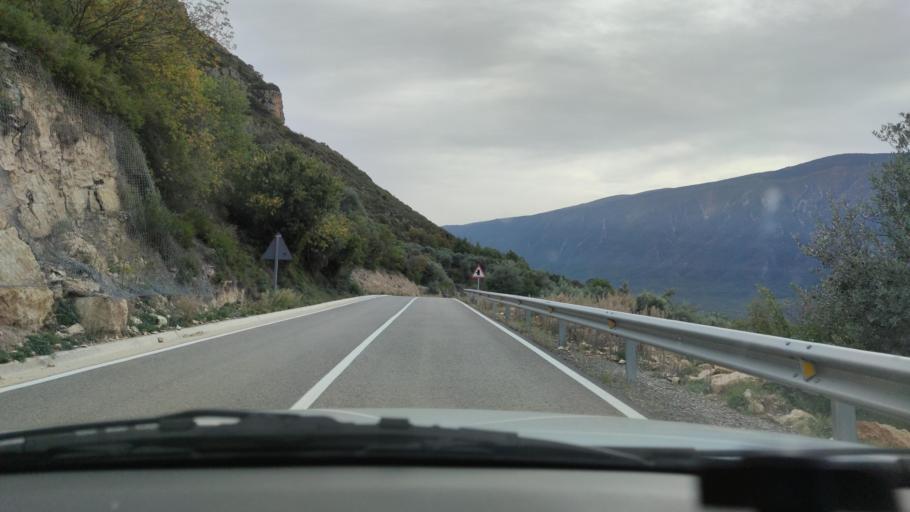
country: ES
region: Catalonia
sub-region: Provincia de Lleida
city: Llimiana
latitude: 42.0703
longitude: 0.9179
